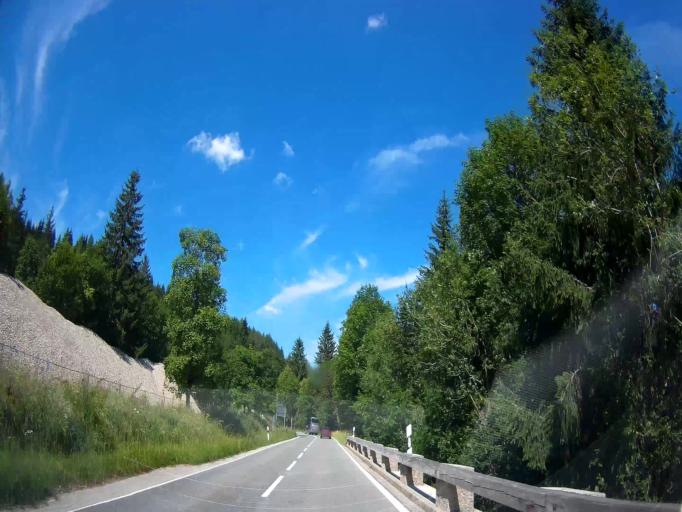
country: DE
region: Bavaria
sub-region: Upper Bavaria
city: Berchtesgaden
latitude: 47.6313
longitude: 13.0545
